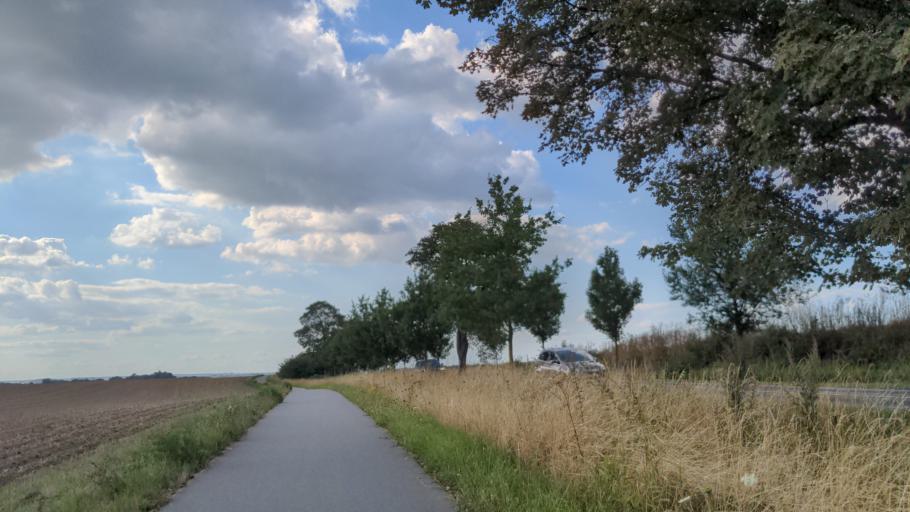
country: DE
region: Mecklenburg-Vorpommern
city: Gramkow
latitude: 53.9118
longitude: 11.3352
